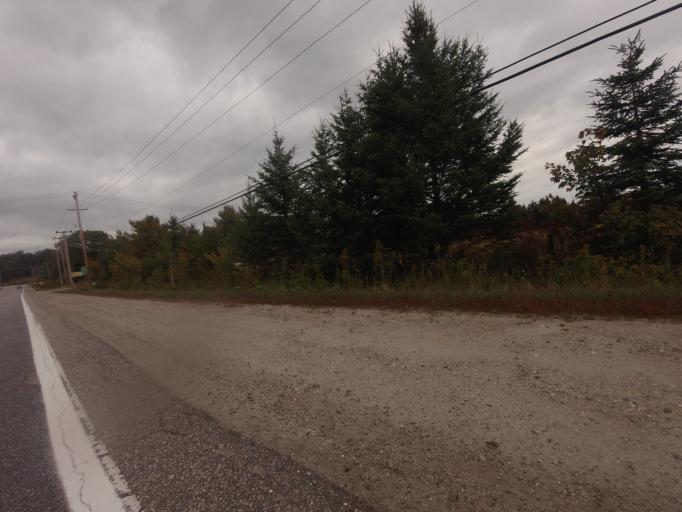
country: CA
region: Quebec
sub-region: Outaouais
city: Wakefield
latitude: 45.9360
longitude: -76.0012
